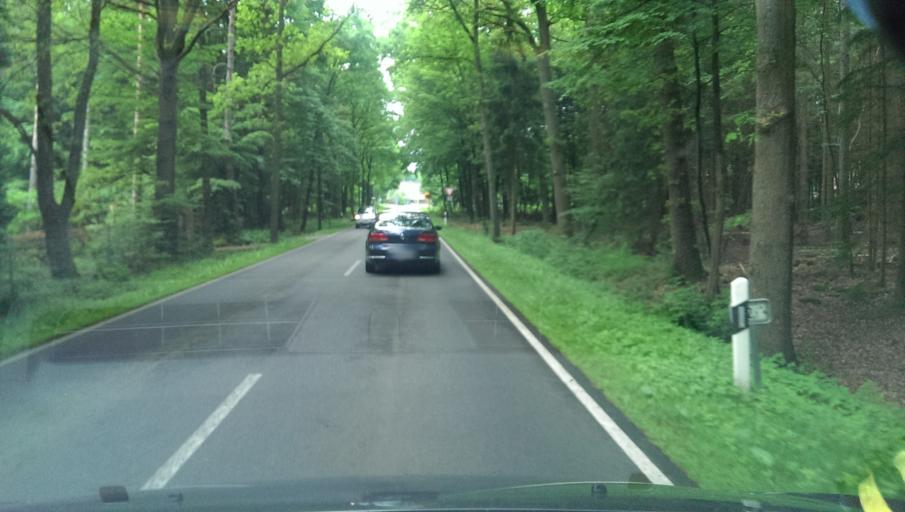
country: DE
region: Lower Saxony
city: Unterluss
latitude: 52.7904
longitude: 10.3865
